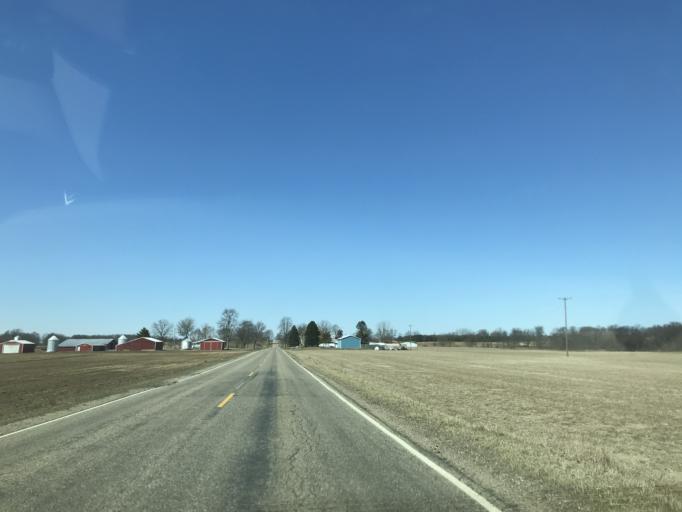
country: US
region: Michigan
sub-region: Hillsdale County
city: Jonesville
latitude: 41.9855
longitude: -84.7017
